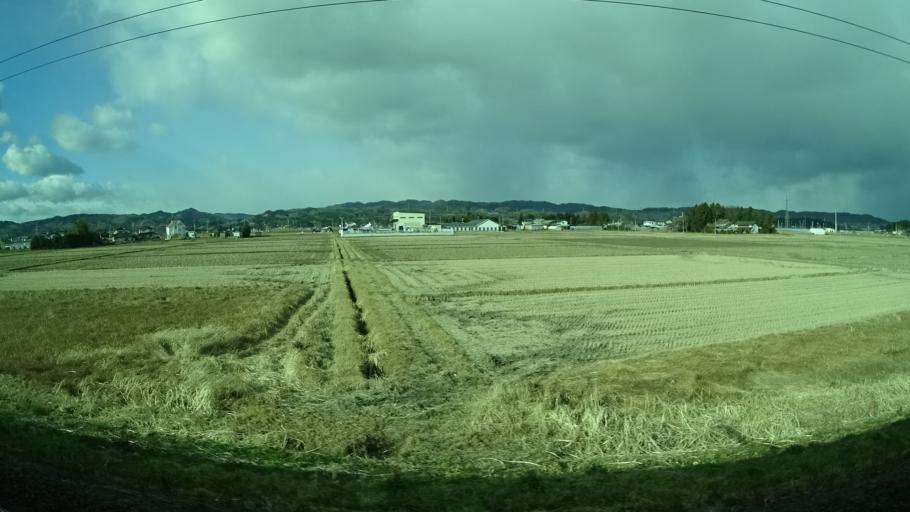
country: JP
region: Miyagi
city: Iwanuma
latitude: 38.1362
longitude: 140.8770
